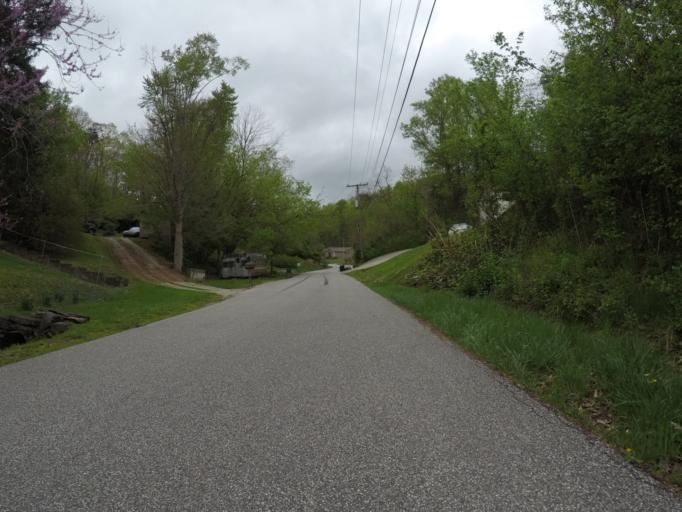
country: US
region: West Virginia
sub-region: Cabell County
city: Barboursville
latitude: 38.4058
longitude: -82.2832
